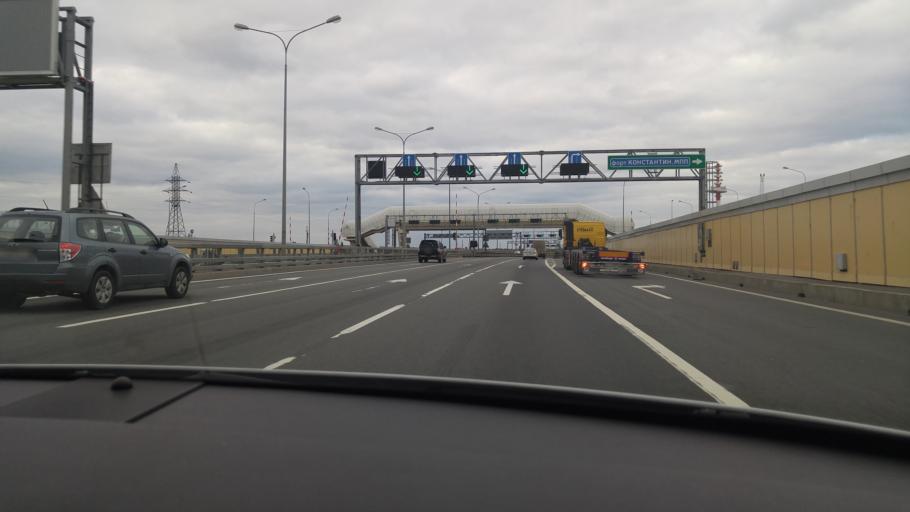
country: RU
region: St.-Petersburg
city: Kronshtadt
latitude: 59.9983
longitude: 29.7010
